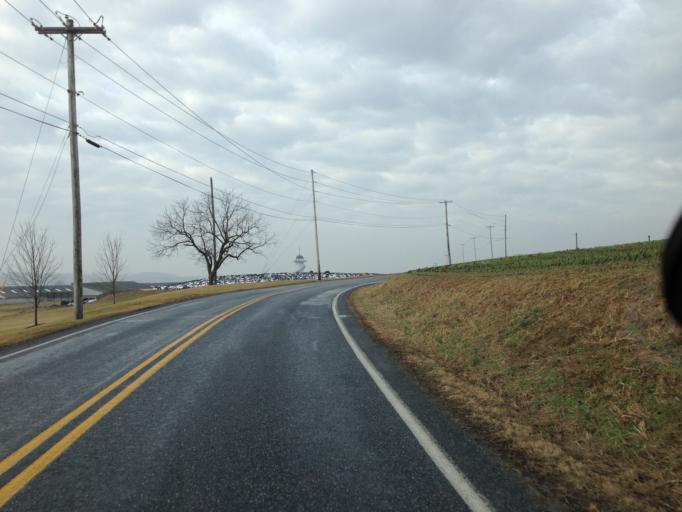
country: US
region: Pennsylvania
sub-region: Lancaster County
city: Penryn
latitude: 40.1735
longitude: -76.3536
